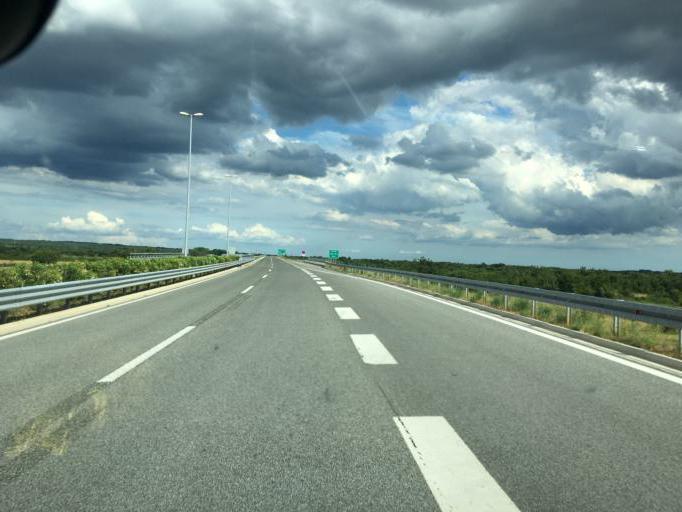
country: HR
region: Istarska
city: Vodnjan
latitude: 44.9848
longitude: 13.8497
